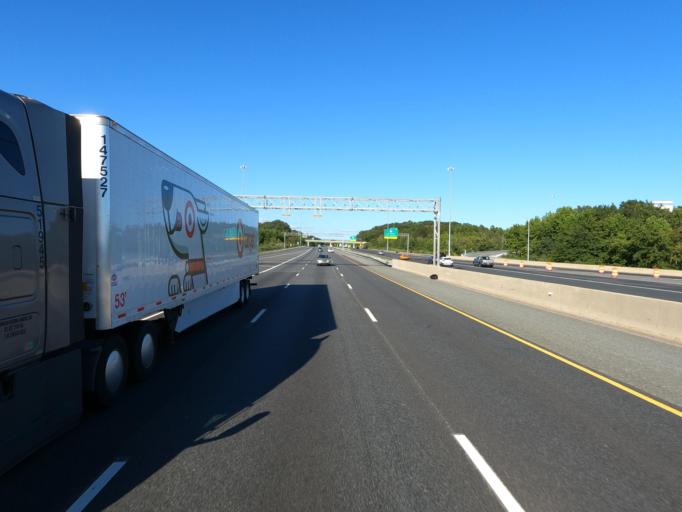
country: US
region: Maryland
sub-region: Cecil County
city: Perryville
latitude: 39.5894
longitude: -76.0709
